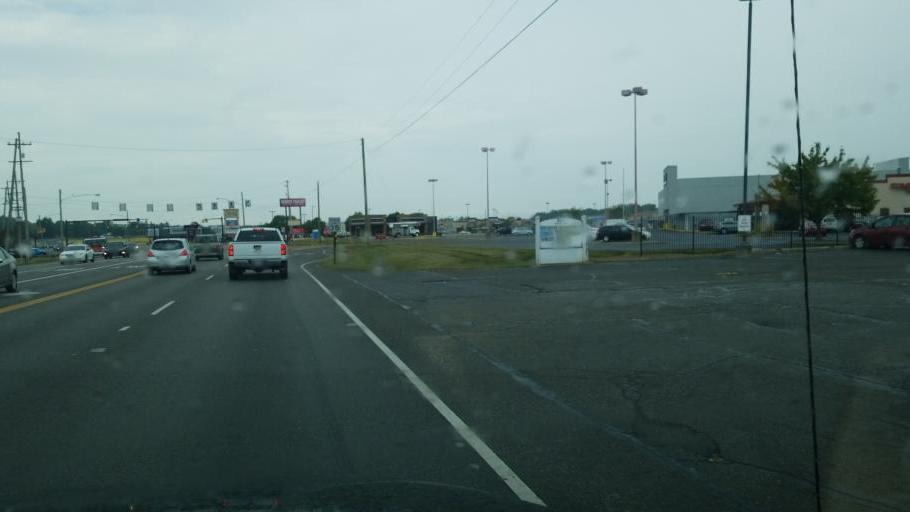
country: US
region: Ohio
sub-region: Licking County
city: Heath
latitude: 40.0281
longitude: -82.4440
